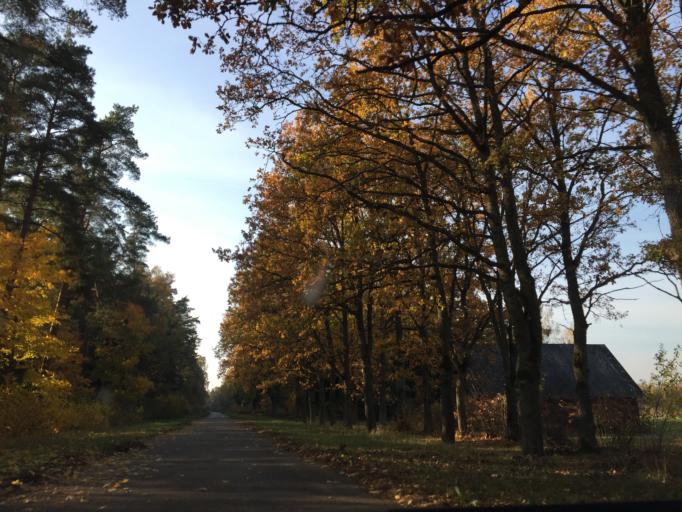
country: LV
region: Skrunda
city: Skrunda
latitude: 56.6785
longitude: 22.1538
